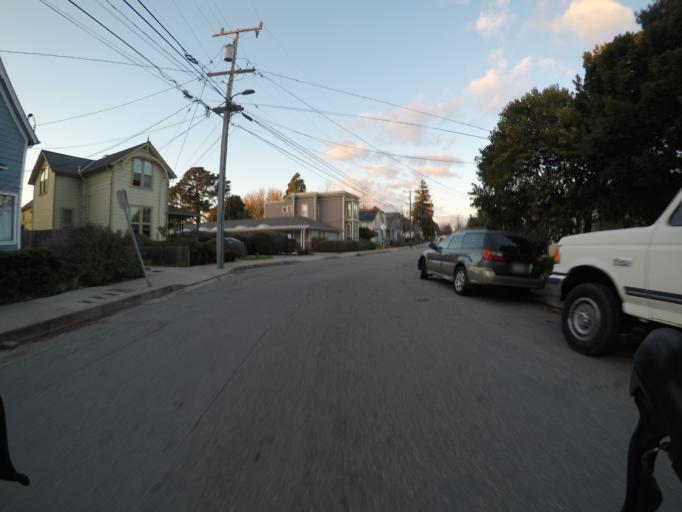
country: US
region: California
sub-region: Santa Cruz County
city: Santa Cruz
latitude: 36.9725
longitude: -122.0218
